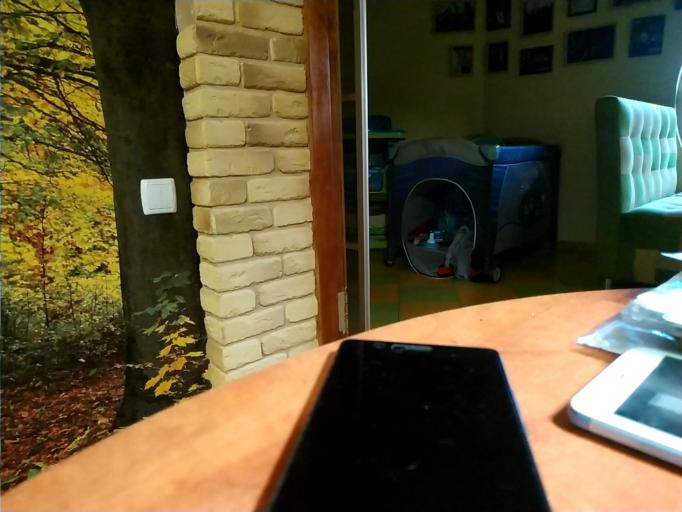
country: RU
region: Orjol
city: Znamenskoye
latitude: 53.5112
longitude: 35.5031
